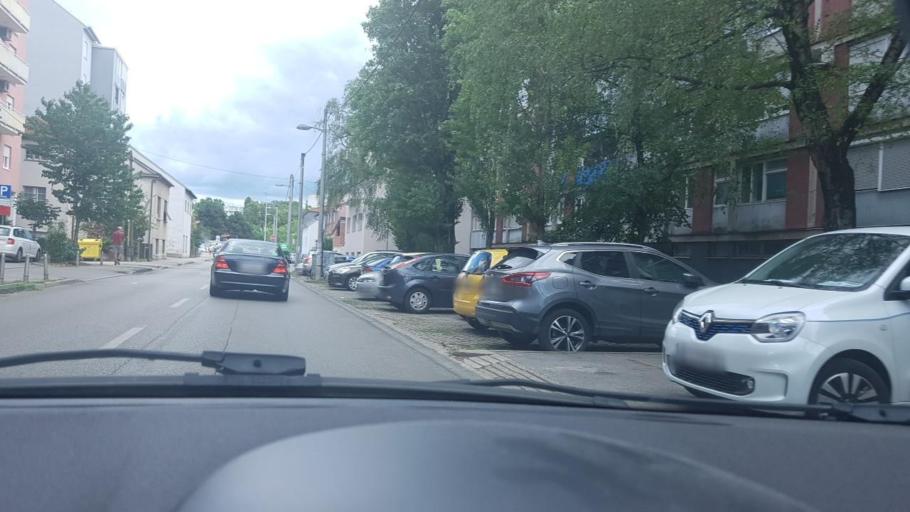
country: HR
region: Grad Zagreb
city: Zagreb - Centar
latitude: 45.7957
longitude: 15.9488
